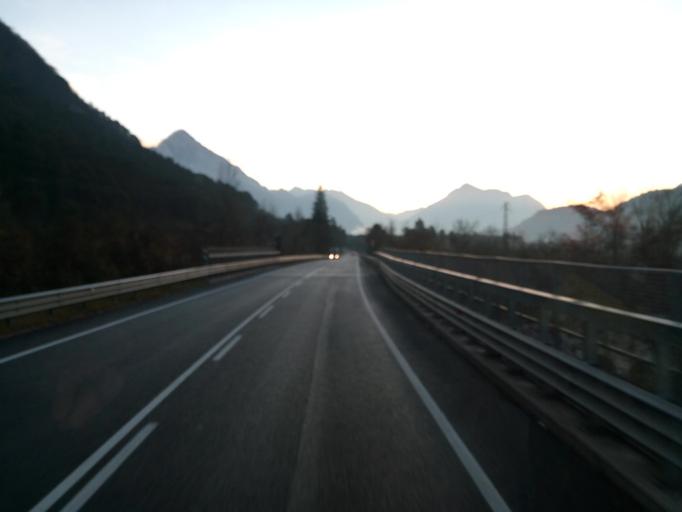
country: IT
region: Friuli Venezia Giulia
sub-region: Provincia di Udine
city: Chiaulis
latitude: 46.4100
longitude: 12.9669
